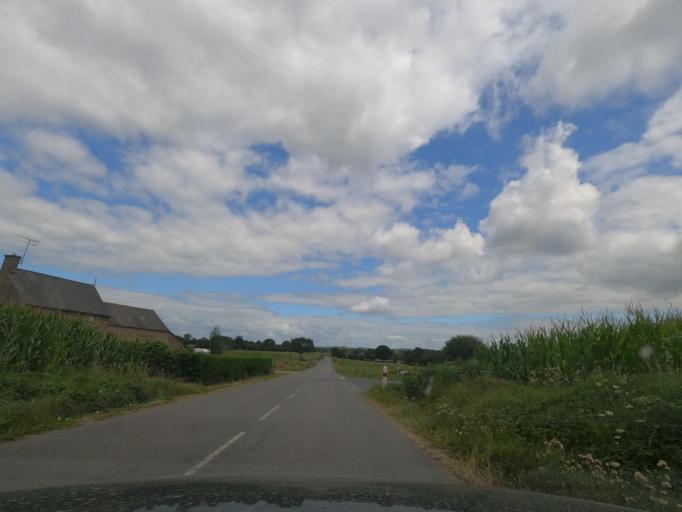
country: FR
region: Brittany
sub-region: Departement d'Ille-et-Vilaine
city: Louvigne-du-Desert
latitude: 48.4413
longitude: -1.0928
